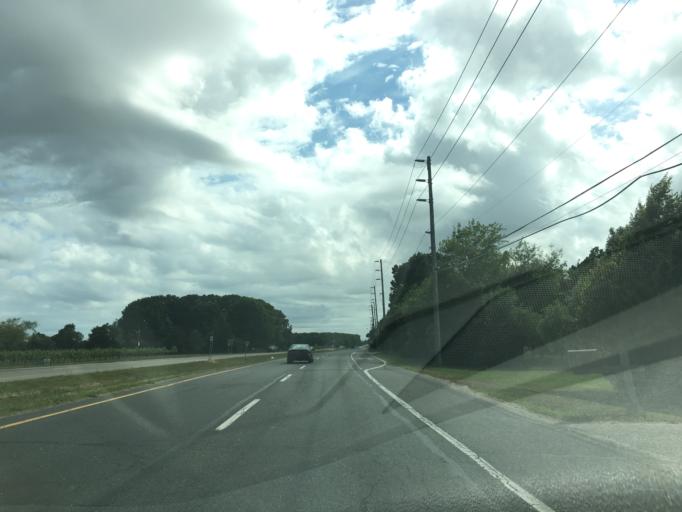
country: US
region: New York
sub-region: Suffolk County
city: Cutchogue
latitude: 41.0220
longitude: -72.5020
